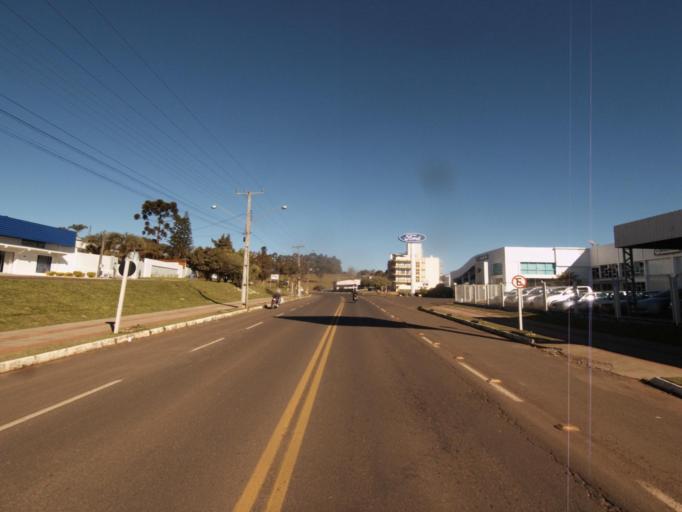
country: AR
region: Misiones
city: Bernardo de Irigoyen
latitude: -26.7474
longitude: -53.5184
